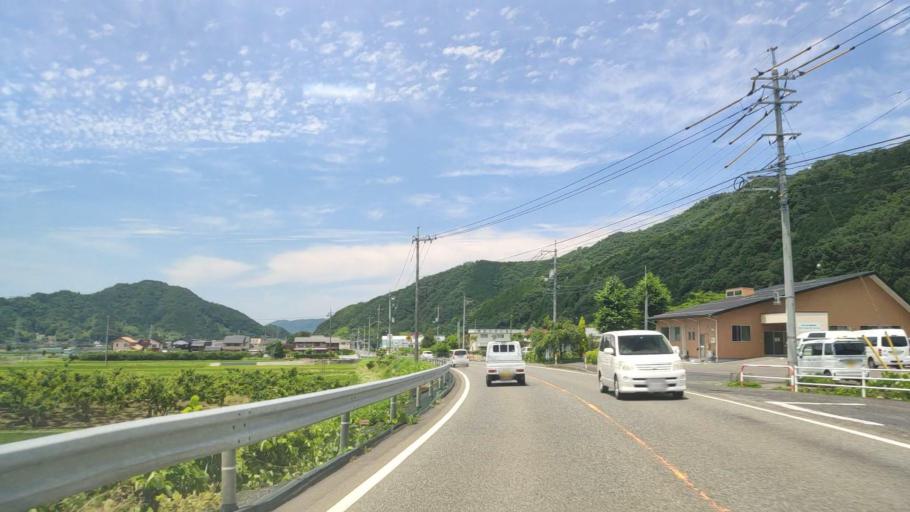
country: JP
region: Tottori
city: Tottori
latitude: 35.3724
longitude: 134.3080
